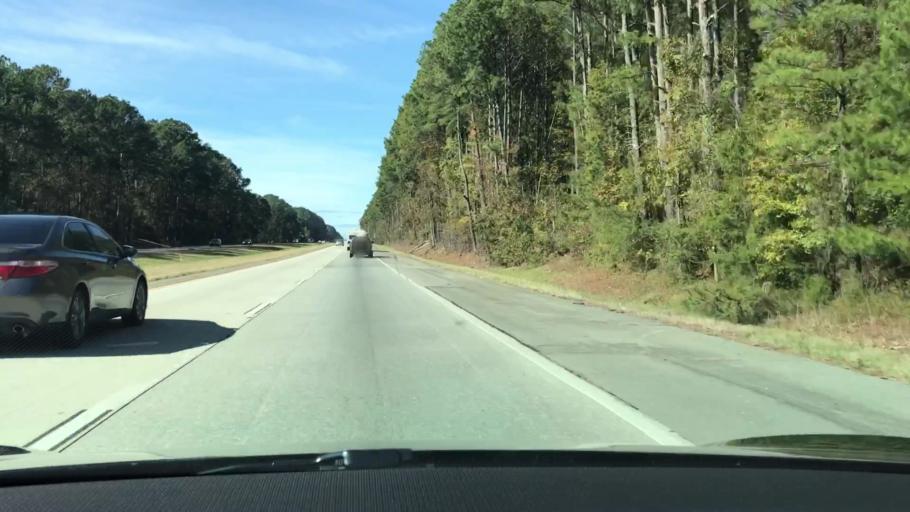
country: US
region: Georgia
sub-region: Greene County
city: Greensboro
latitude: 33.5490
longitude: -83.1476
